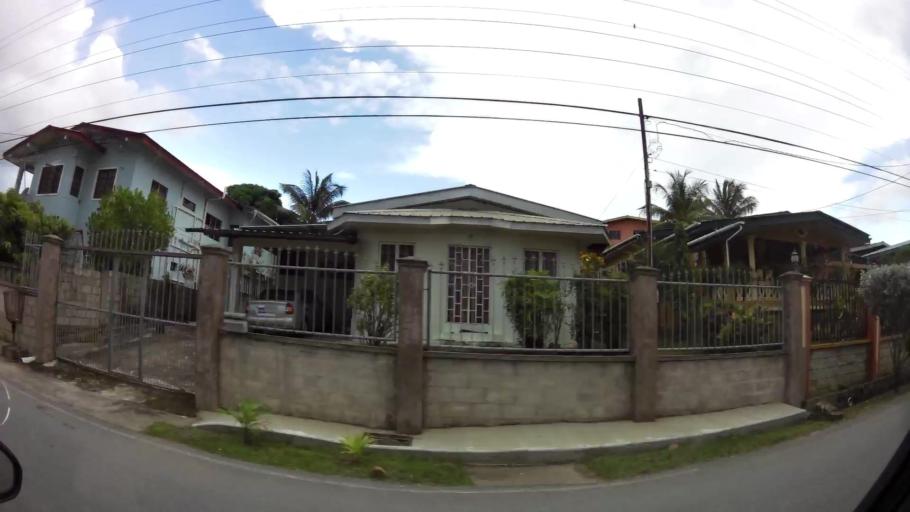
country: TT
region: City of San Fernando
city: Mon Repos
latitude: 10.2537
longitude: -61.4569
